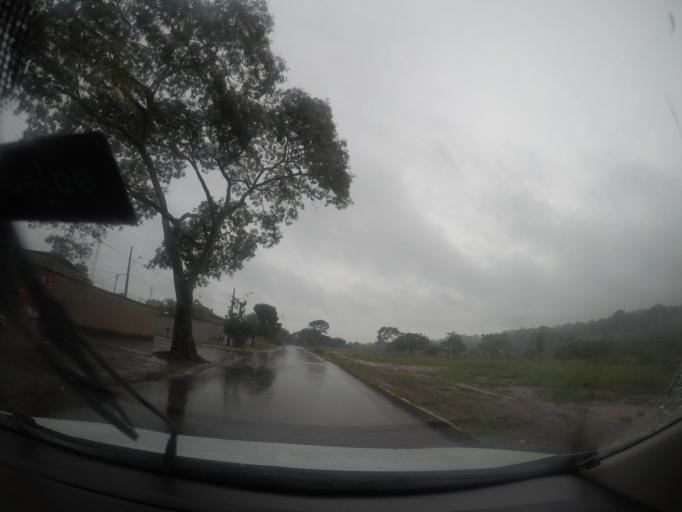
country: BR
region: Goias
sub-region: Goiania
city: Goiania
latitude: -16.5998
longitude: -49.3514
